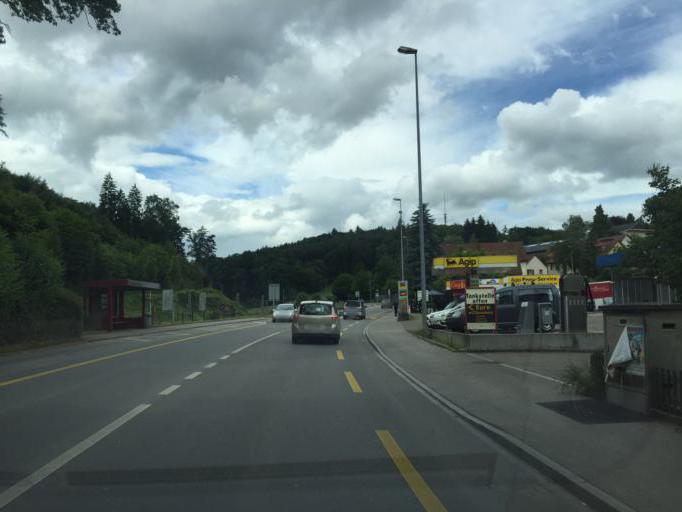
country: CH
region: Schaffhausen
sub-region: Bezirk Schaffhausen
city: Neuhausen
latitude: 47.6861
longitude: 8.6113
